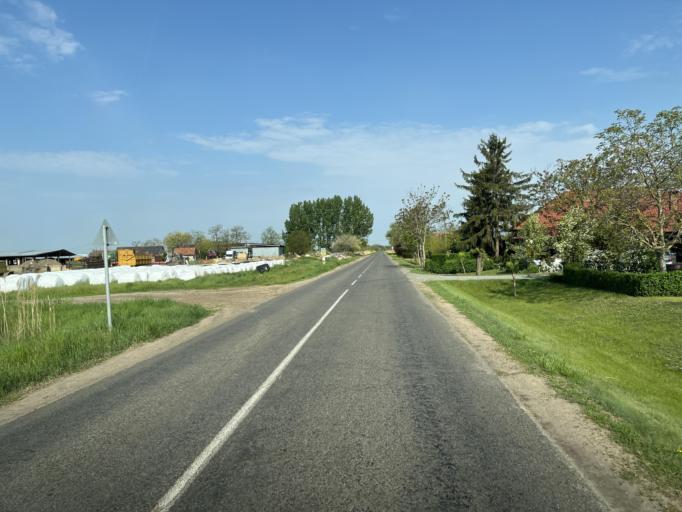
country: HU
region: Pest
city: Jaszkarajeno
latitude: 47.0445
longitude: 20.0900
